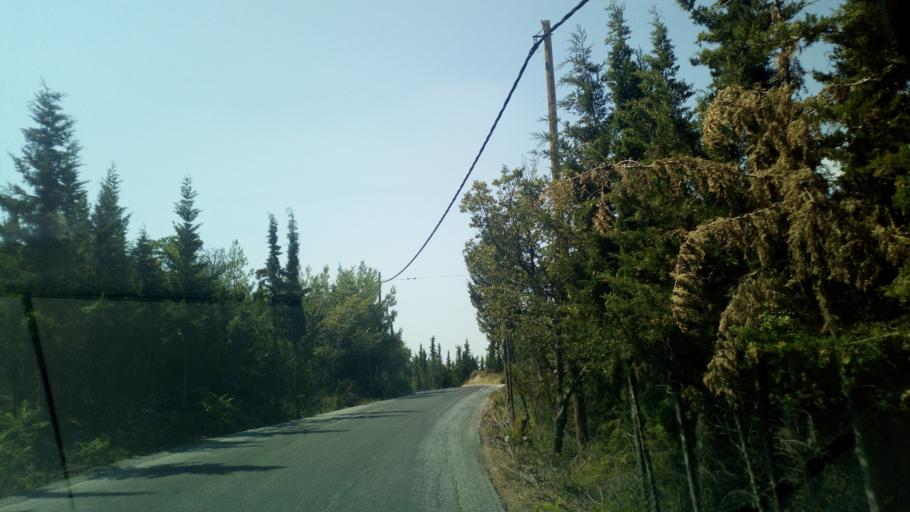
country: GR
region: Central Macedonia
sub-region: Nomos Thessalonikis
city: Pefka
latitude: 40.6423
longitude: 23.0039
